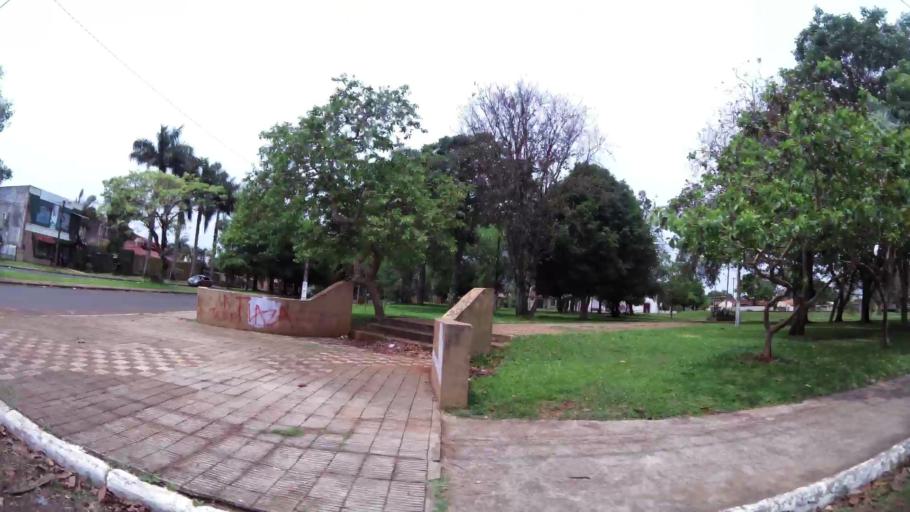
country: PY
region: Alto Parana
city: Presidente Franco
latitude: -25.5523
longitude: -54.6262
